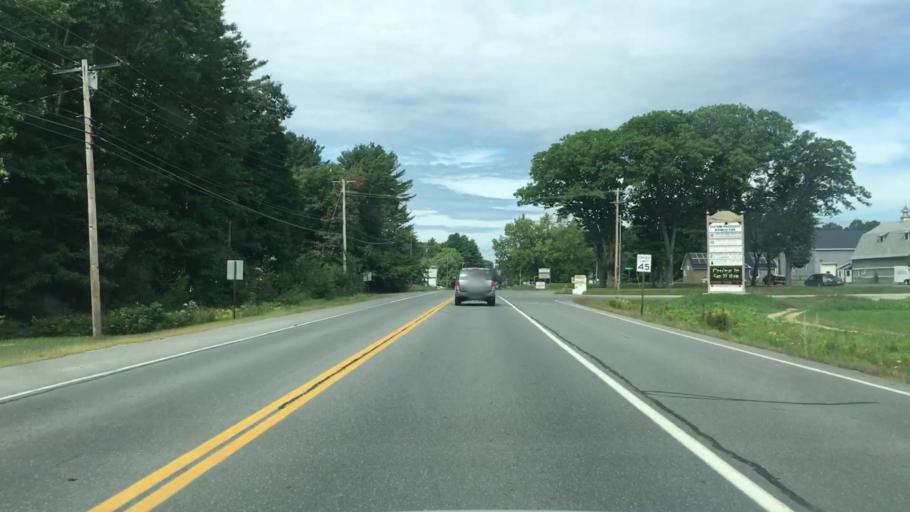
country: US
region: Maine
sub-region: Piscataquis County
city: Milo
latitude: 45.2654
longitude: -68.9932
